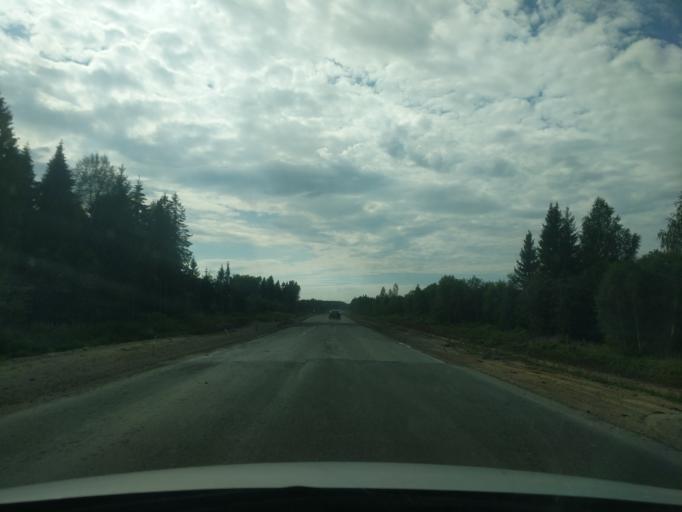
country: RU
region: Kostroma
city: Sudislavl'
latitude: 57.8555
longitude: 41.6045
